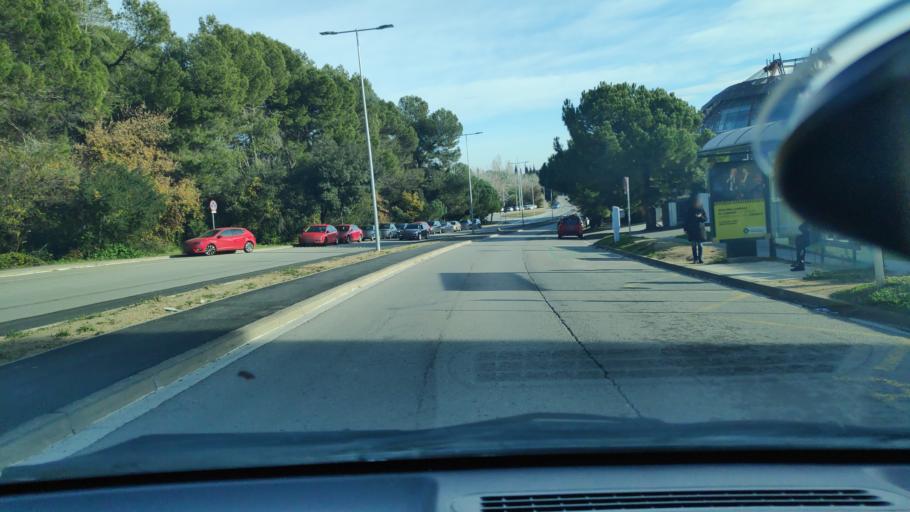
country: ES
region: Catalonia
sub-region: Provincia de Barcelona
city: Rubi
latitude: 41.4922
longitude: 2.0564
